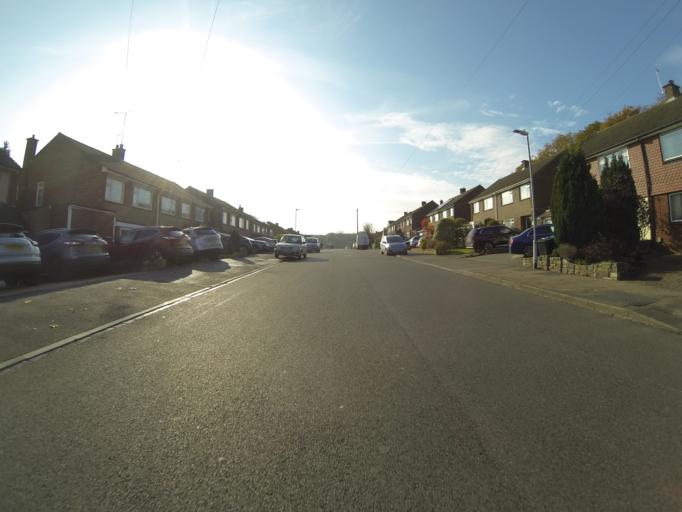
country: GB
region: England
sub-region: Greater London
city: Bexley
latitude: 51.4247
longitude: 0.1662
